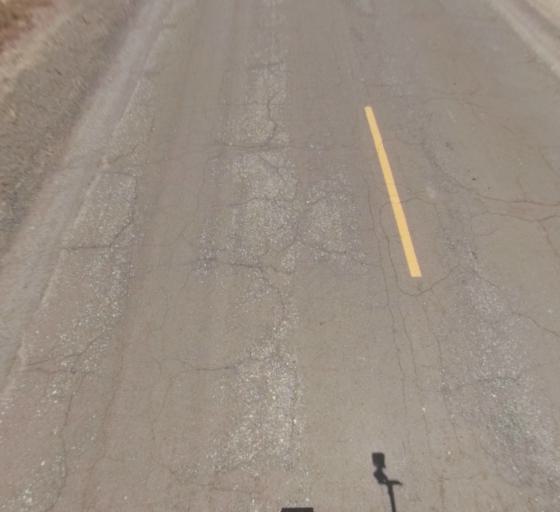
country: US
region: California
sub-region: Madera County
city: Parksdale
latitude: 36.8855
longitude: -119.9837
